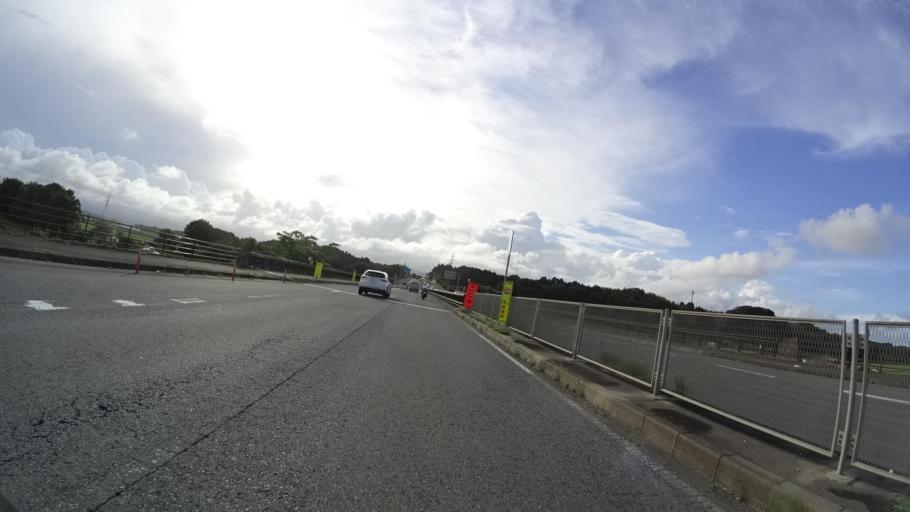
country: JP
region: Mie
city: Suzuka
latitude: 34.8801
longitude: 136.5195
